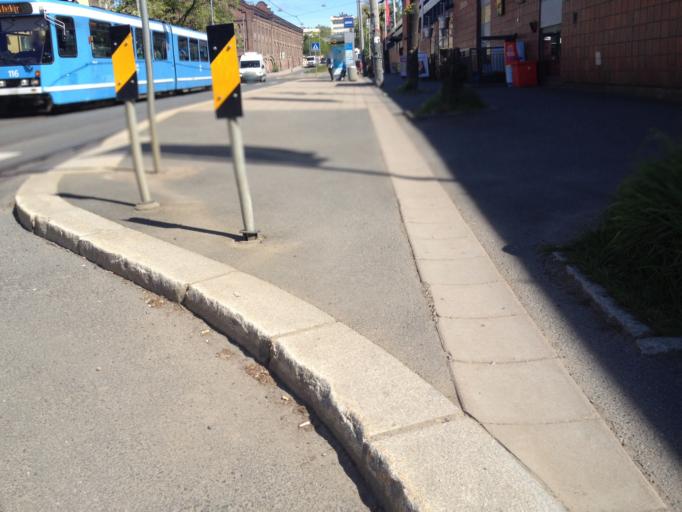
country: NO
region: Oslo
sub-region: Oslo
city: Oslo
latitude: 59.9383
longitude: 10.7686
